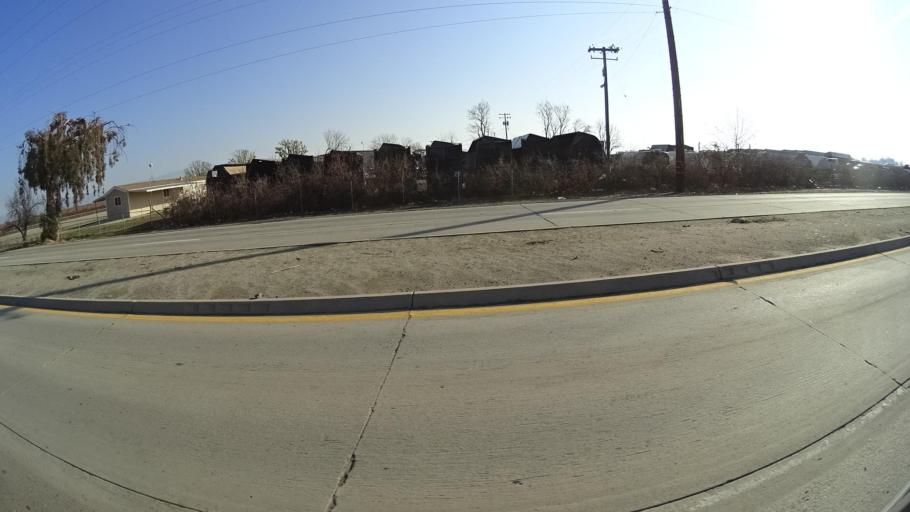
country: US
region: California
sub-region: Kern County
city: Greenfield
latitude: 35.2445
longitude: -119.0032
